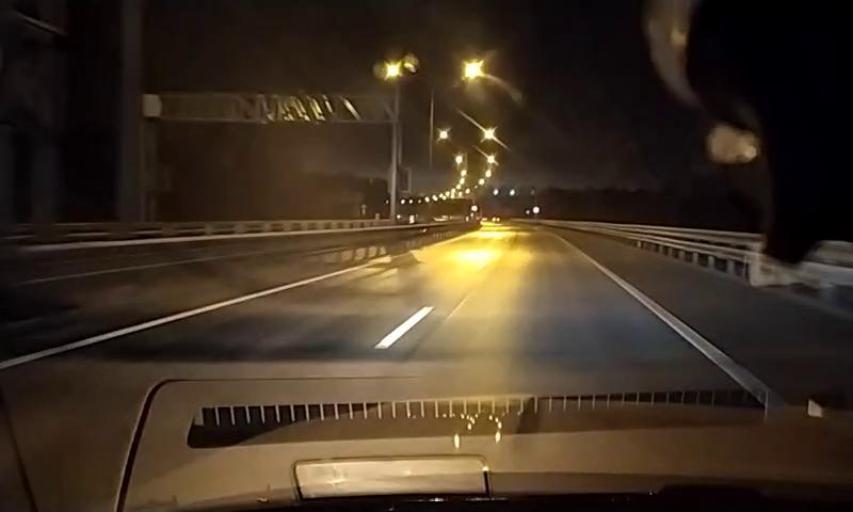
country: RU
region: Leningrad
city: Luppolovo
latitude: 60.1608
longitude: 30.3530
